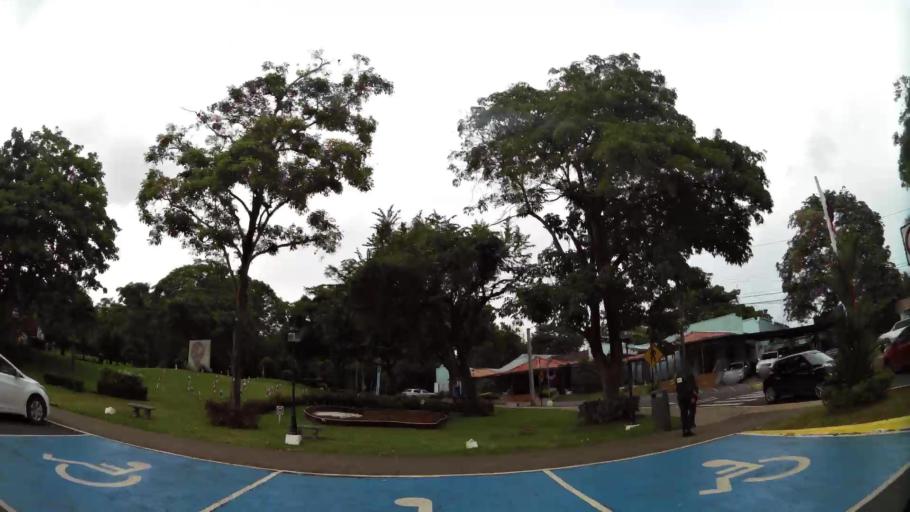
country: PA
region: Panama
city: Panama
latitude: 8.9977
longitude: -79.5067
